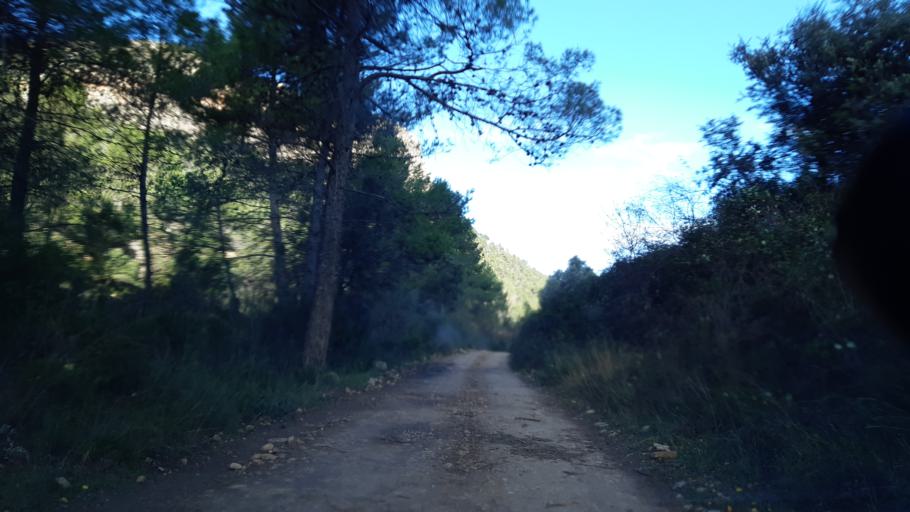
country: ES
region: Aragon
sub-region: Provincia de Teruel
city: Lledo
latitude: 40.8666
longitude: 0.2543
